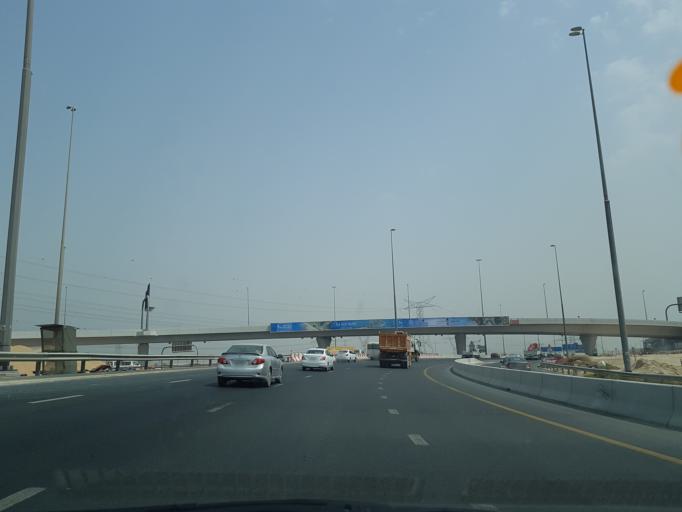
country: AE
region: Ash Shariqah
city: Sharjah
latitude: 25.2146
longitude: 55.4047
